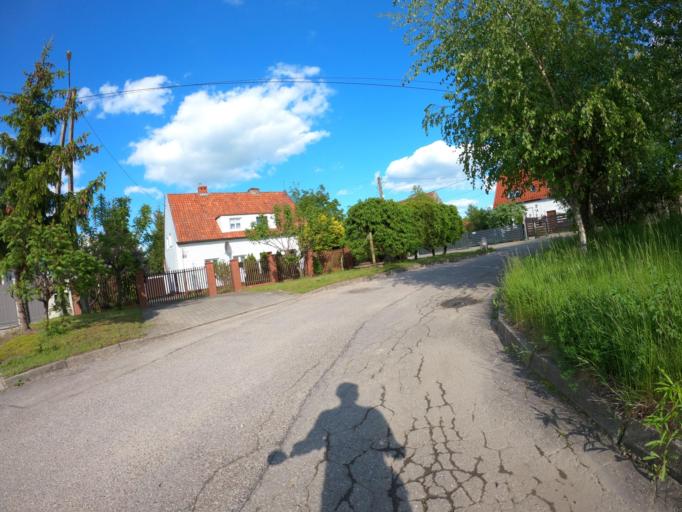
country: PL
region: Warmian-Masurian Voivodeship
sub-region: Powiat lidzbarski
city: Lidzbark Warminski
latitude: 54.1318
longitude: 20.6000
